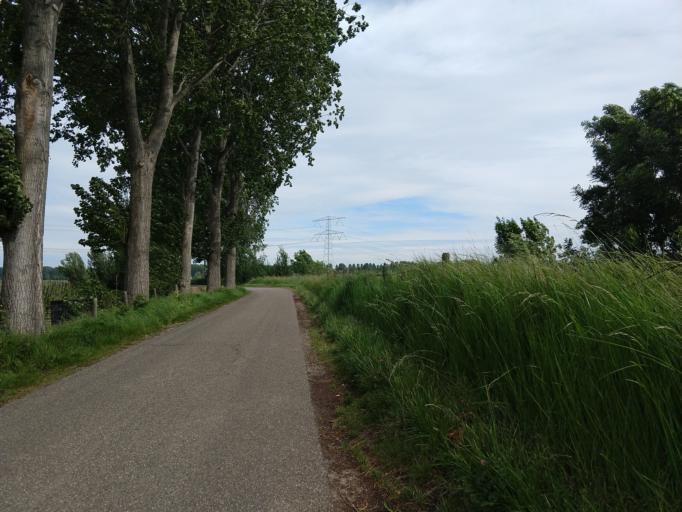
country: NL
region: Zeeland
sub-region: Gemeente Goes
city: Goes
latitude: 51.4462
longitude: 3.9198
